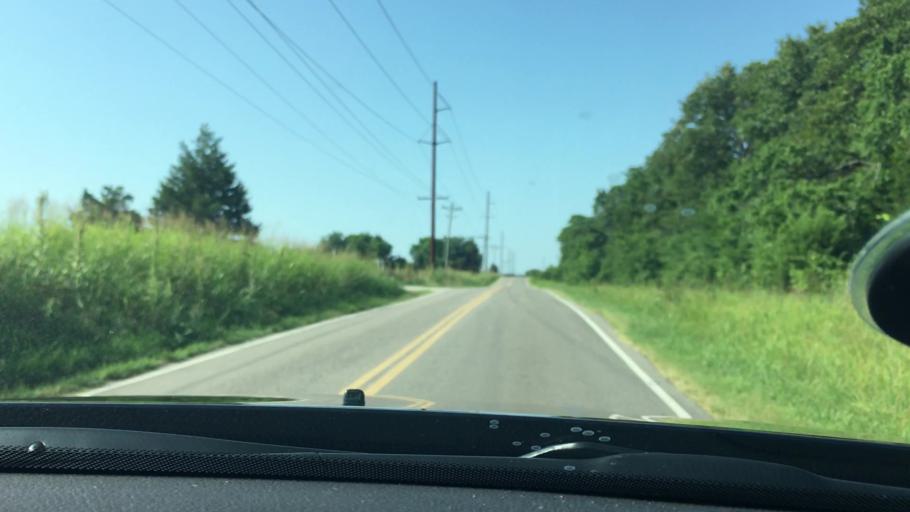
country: US
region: Oklahoma
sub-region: Pontotoc County
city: Ada
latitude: 34.8038
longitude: -96.6348
